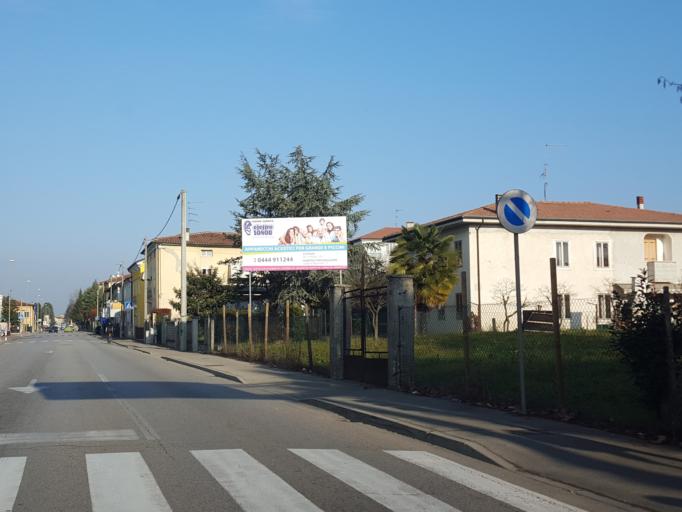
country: IT
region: Veneto
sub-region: Provincia di Vicenza
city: Vicenza
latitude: 45.5324
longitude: 11.5217
